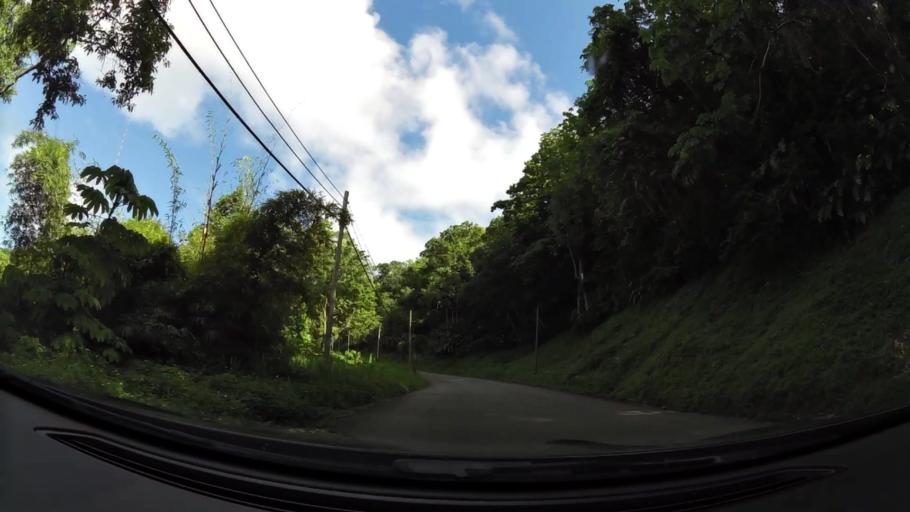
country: TT
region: Eastern Tobago
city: Roxborough
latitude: 11.3184
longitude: -60.5452
